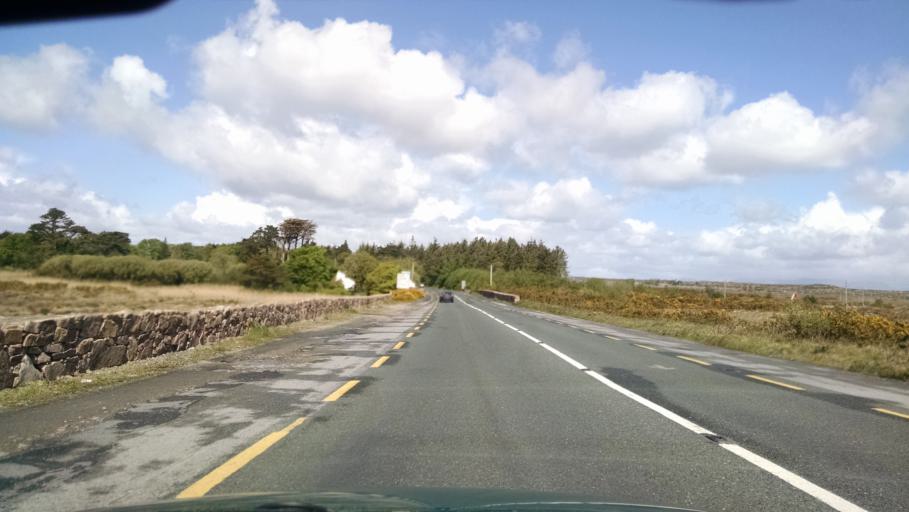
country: IE
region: Connaught
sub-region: County Galway
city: Oughterard
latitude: 53.2775
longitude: -9.5312
